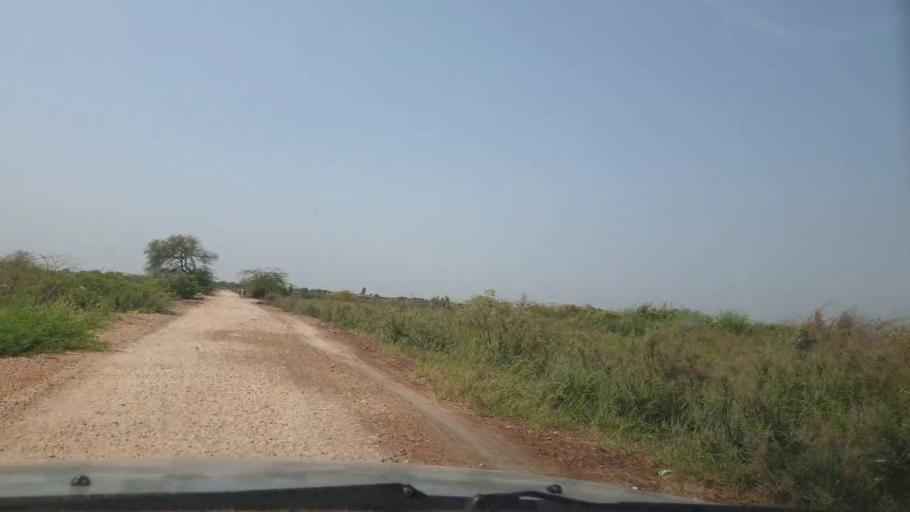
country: PK
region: Sindh
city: Tando Ghulam Ali
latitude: 25.1141
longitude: 68.7921
